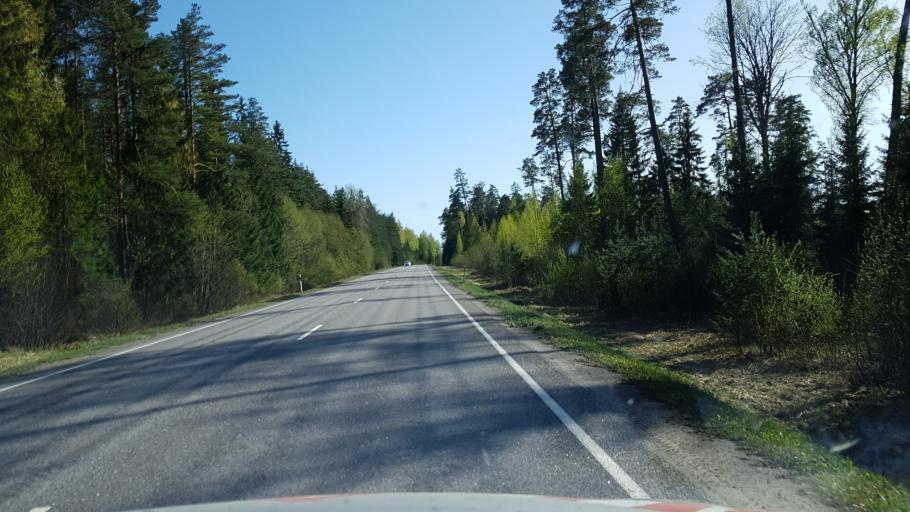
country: EE
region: Paernumaa
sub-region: Saarde vald
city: Kilingi-Nomme
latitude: 58.1883
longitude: 25.0548
